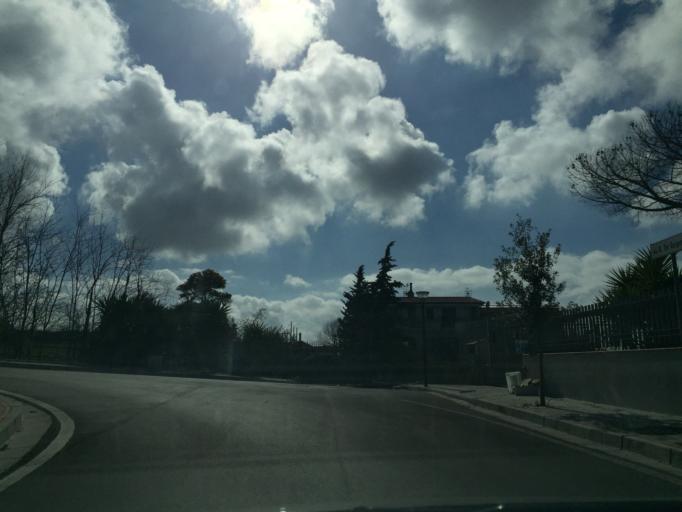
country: IT
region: Campania
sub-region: Provincia di Napoli
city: Pollena Trocchia
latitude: 40.8499
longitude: 14.3799
